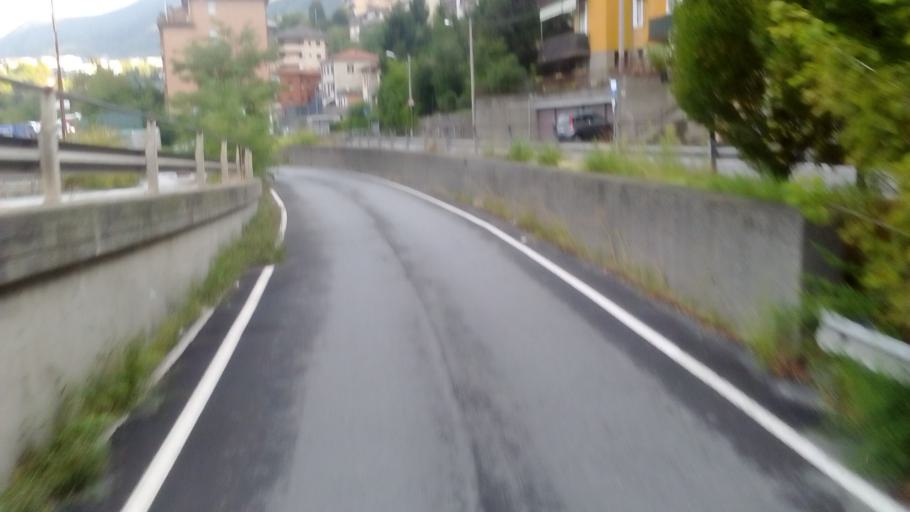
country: CH
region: Ticino
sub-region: Mendrisio District
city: Chiasso
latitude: 45.8348
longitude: 9.0387
